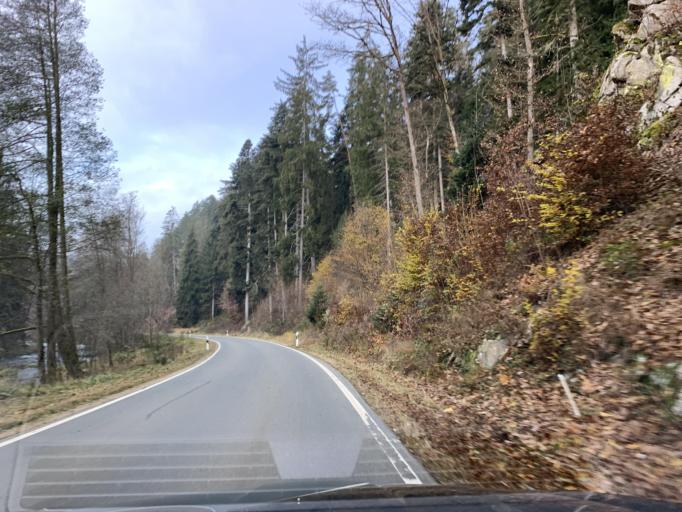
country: DE
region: Bavaria
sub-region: Upper Palatinate
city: Thanstein
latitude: 49.3630
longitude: 12.4428
